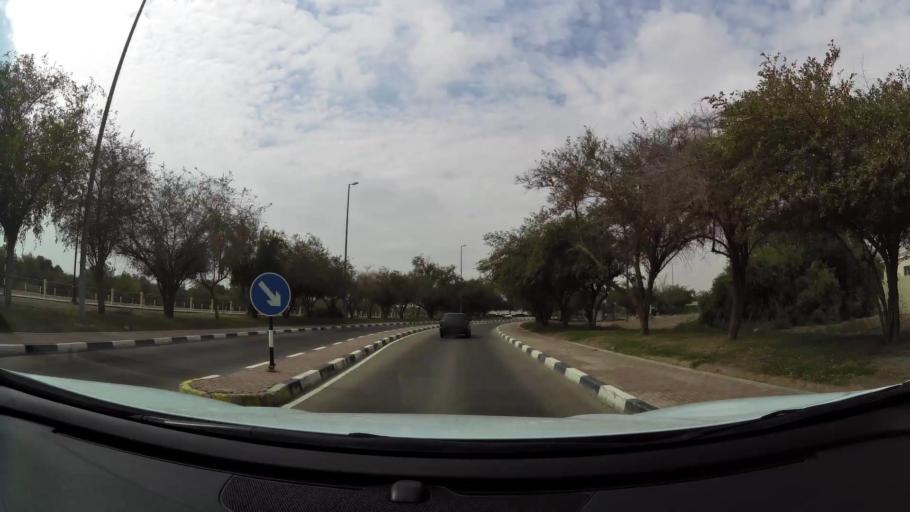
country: OM
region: Al Buraimi
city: Al Buraymi
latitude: 24.2079
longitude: 55.8015
